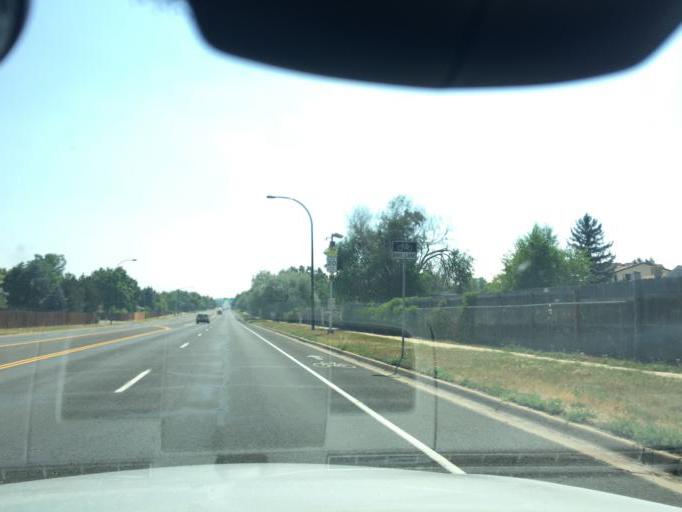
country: US
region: Colorado
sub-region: Broomfield County
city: Broomfield
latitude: 39.8998
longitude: -105.0653
